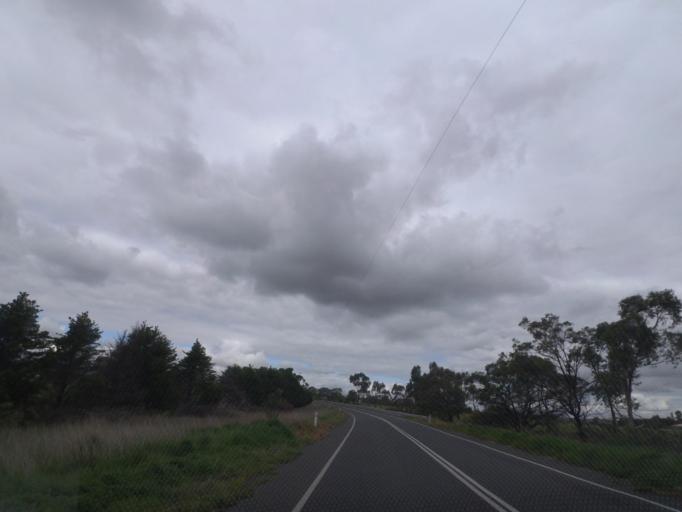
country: AU
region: Victoria
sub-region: Hume
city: Craigieburn
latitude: -37.3912
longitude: 144.8999
